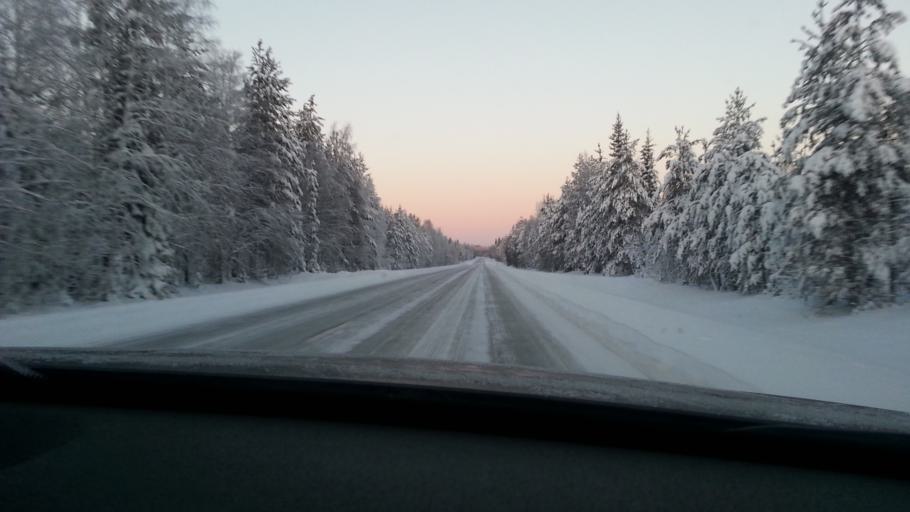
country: FI
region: Lapland
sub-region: Tunturi-Lappi
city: Kittilae
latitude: 67.2229
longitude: 24.9235
